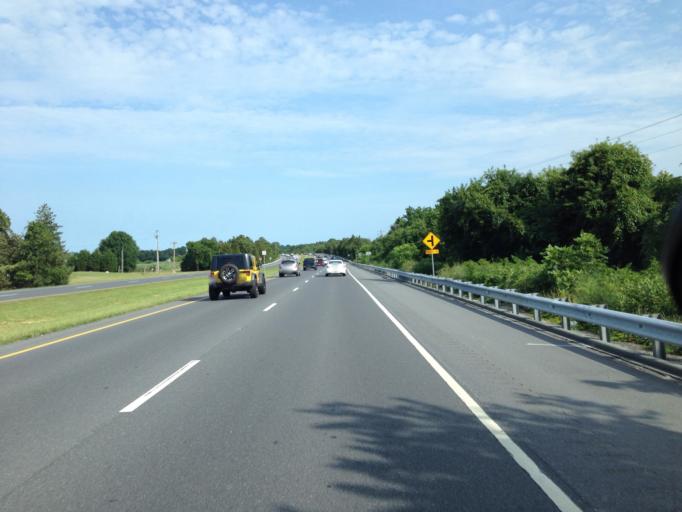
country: US
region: Delaware
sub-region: Sussex County
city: Milton
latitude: 38.7946
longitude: -75.2571
